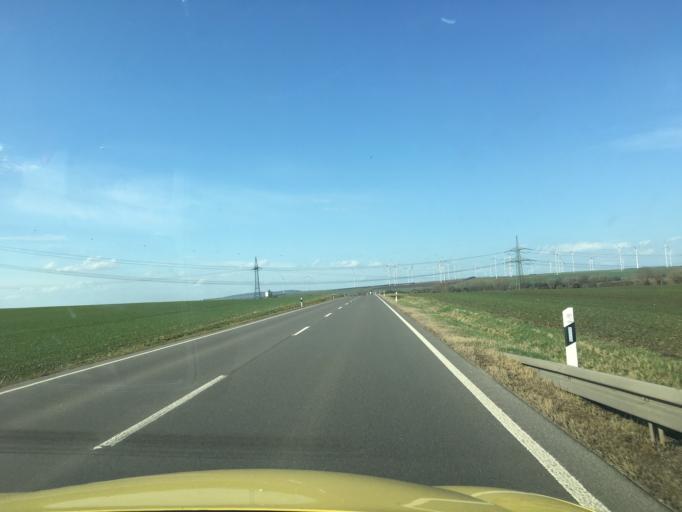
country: DE
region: Thuringia
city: Olbersleben
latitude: 51.1314
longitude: 11.3412
